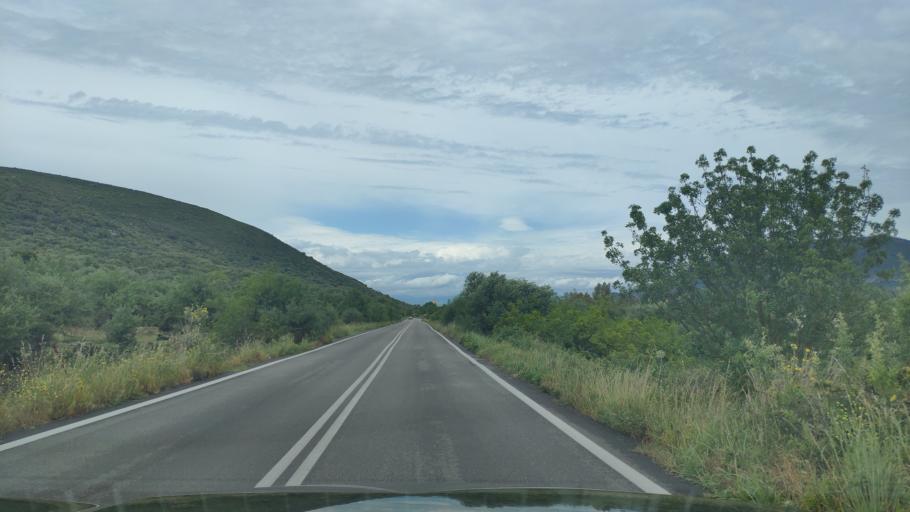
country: GR
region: West Greece
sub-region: Nomos Aitolias kai Akarnanias
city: Vonitsa
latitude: 38.8811
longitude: 20.8968
